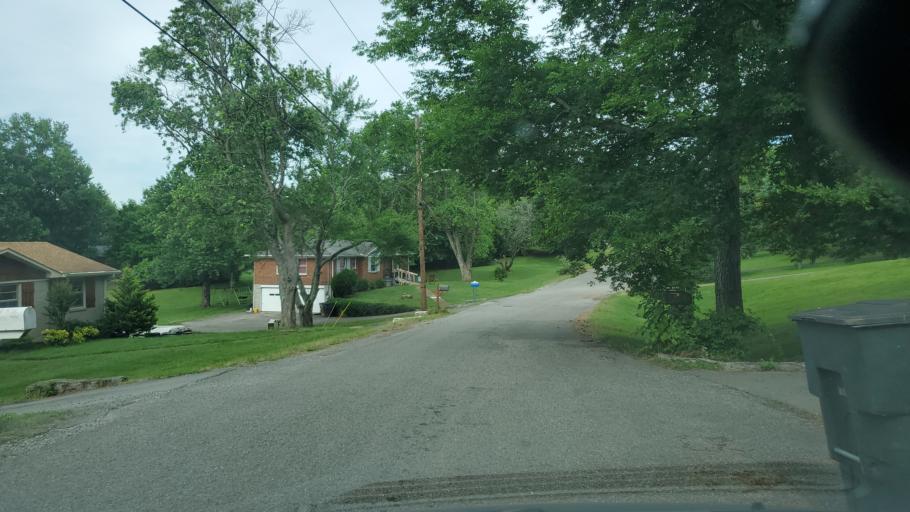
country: US
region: Tennessee
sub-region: Davidson County
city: Lakewood
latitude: 36.2182
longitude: -86.6858
